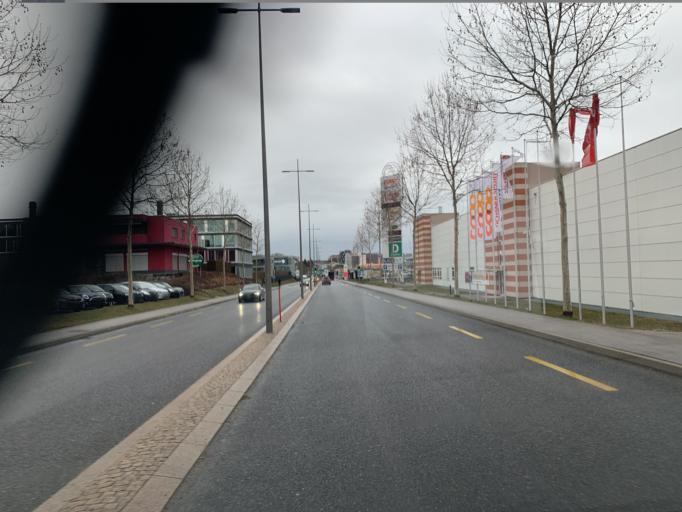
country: CH
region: Fribourg
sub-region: Sarine District
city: Fribourg
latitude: 46.8203
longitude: 7.1530
